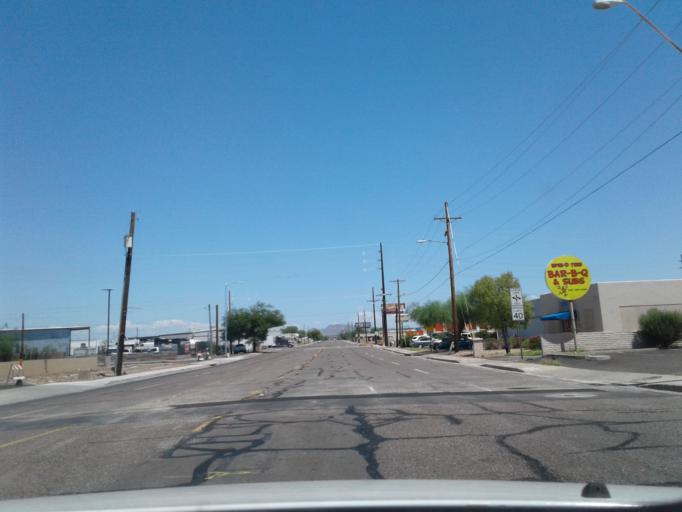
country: US
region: Arizona
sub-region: Maricopa County
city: Tempe Junction
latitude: 33.4145
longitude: -111.9954
